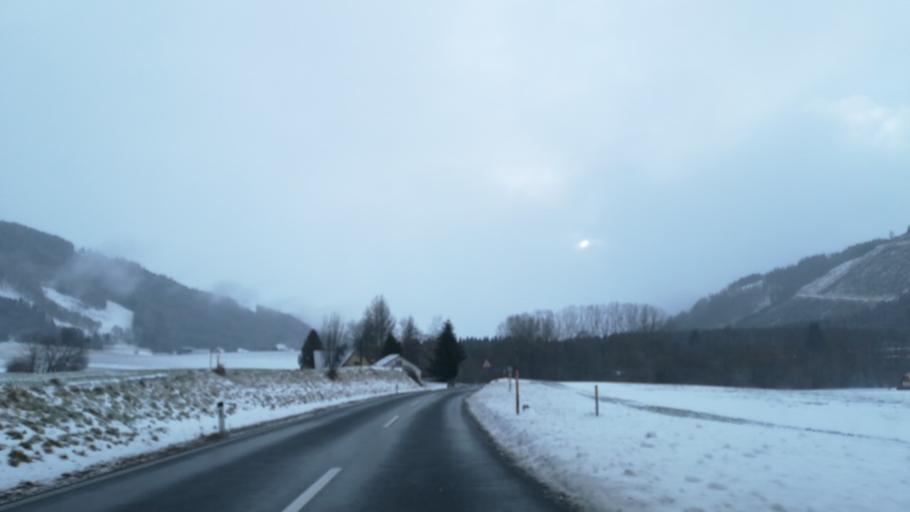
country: AT
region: Styria
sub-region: Politischer Bezirk Murtal
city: Poels
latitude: 47.2209
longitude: 14.6005
